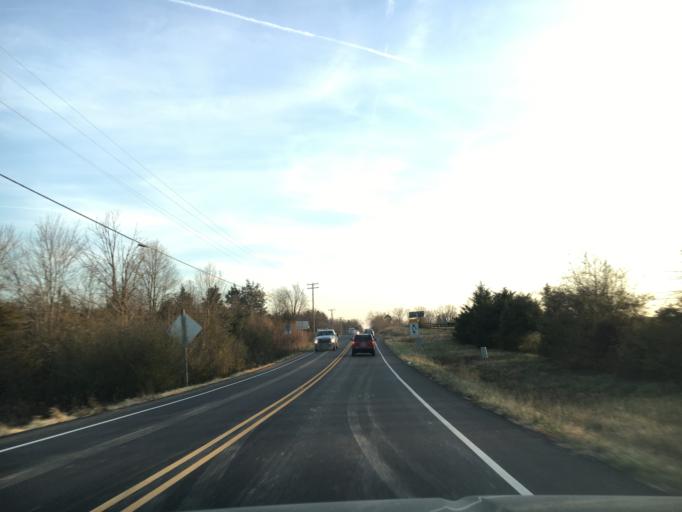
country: US
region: Virginia
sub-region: Orange County
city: Orange
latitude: 38.2643
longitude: -77.9566
